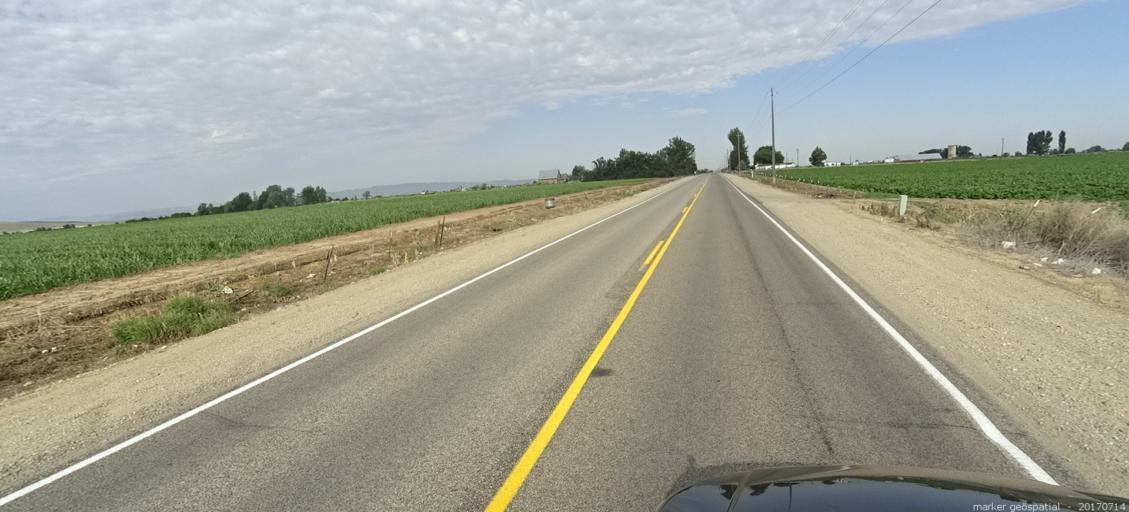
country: US
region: Idaho
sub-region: Ada County
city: Kuna
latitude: 43.4884
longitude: -116.4405
